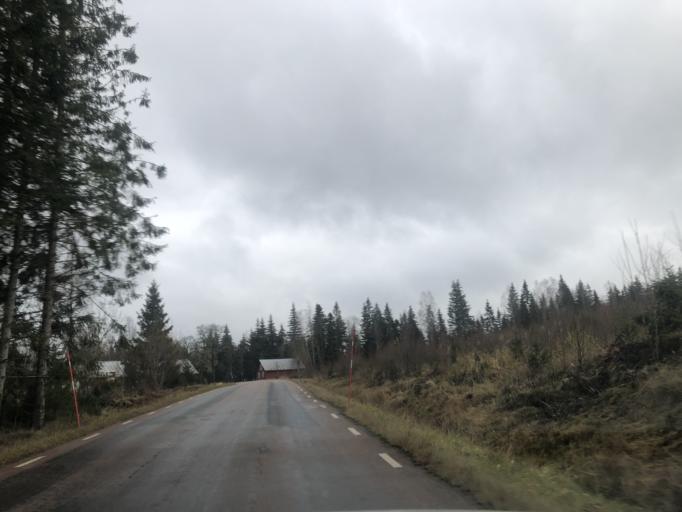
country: SE
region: Vaestra Goetaland
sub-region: Ulricehamns Kommun
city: Ulricehamn
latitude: 57.8304
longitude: 13.4997
